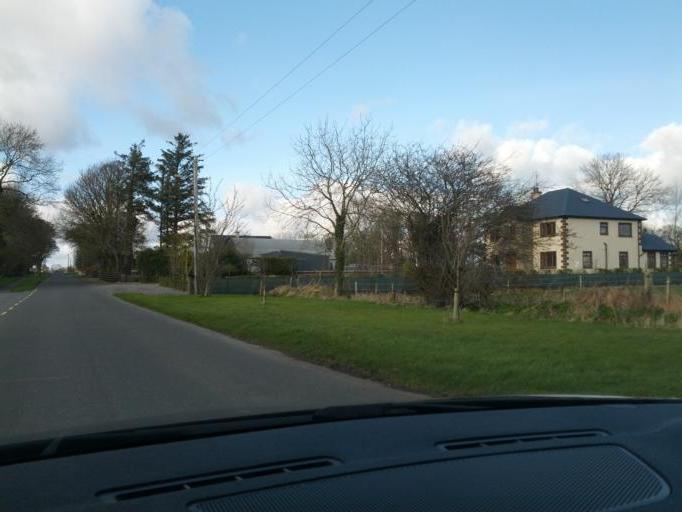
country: IE
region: Connaught
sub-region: County Galway
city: Athenry
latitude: 53.4817
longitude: -8.5693
